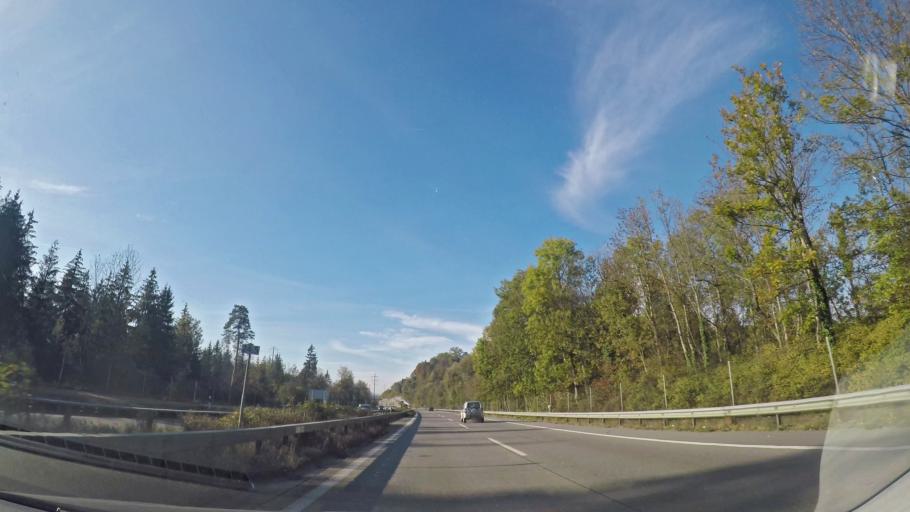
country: CH
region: Bern
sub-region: Thun District
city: Heimberg
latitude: 46.7918
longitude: 7.5947
